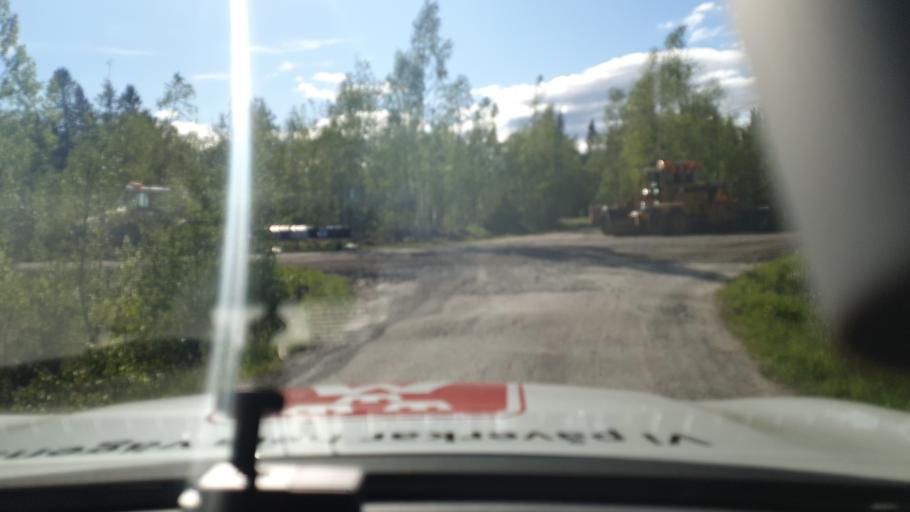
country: SE
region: Vaesterbotten
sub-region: Umea Kommun
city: Taftea
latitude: 63.7664
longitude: 20.4491
